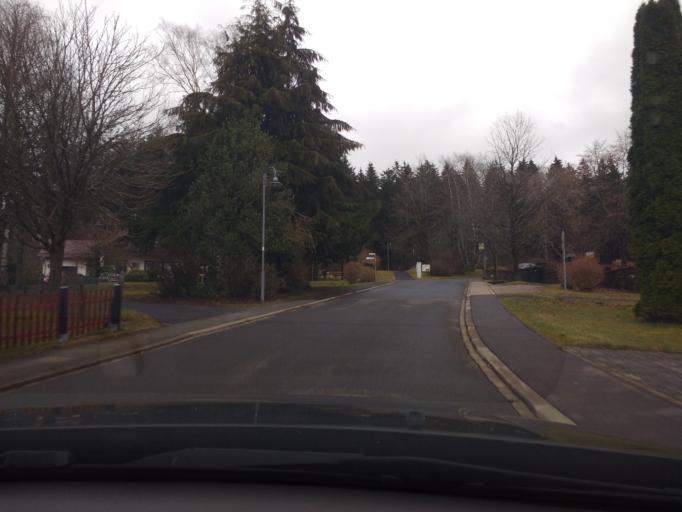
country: DE
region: Rheinland-Pfalz
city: Damflos
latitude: 49.6670
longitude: 6.9873
